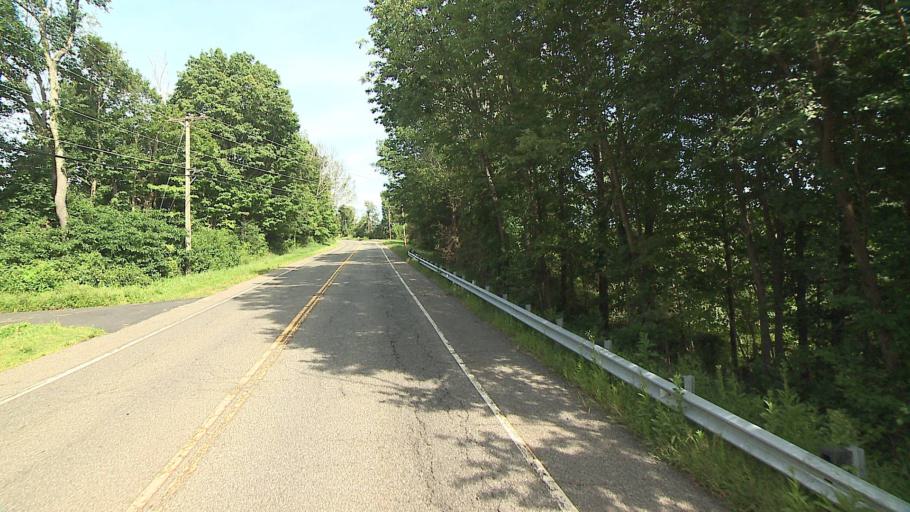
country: US
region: Connecticut
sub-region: Litchfield County
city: Litchfield
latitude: 41.7226
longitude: -73.1465
